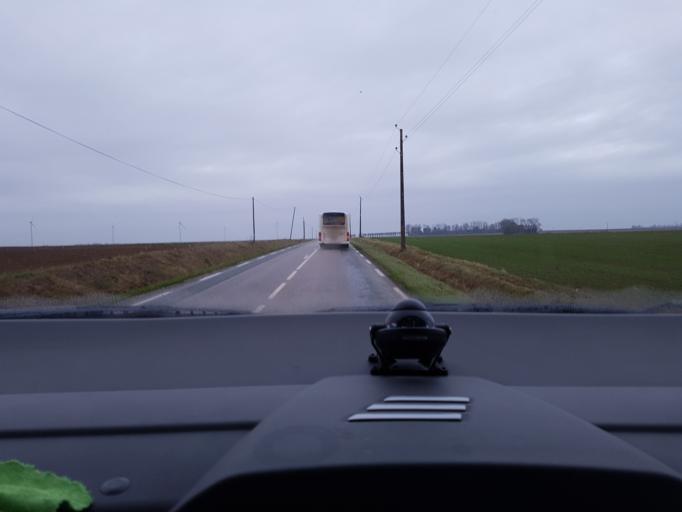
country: FR
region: Haute-Normandie
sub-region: Departement de l'Eure
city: Beaumont-le-Roger
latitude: 49.0902
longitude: 0.7980
